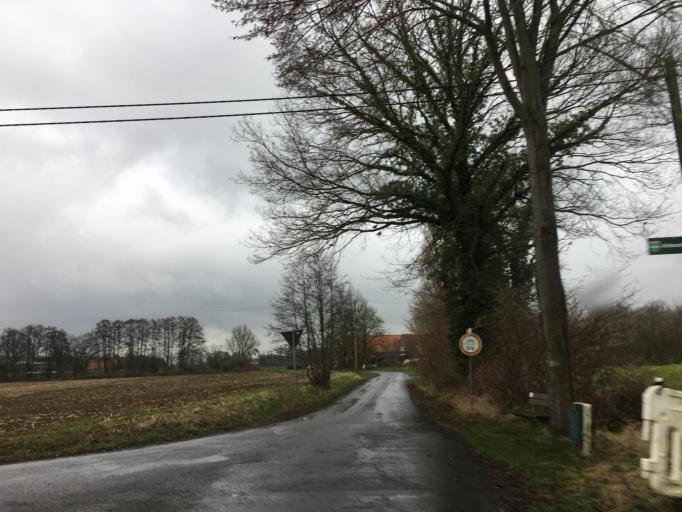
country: DE
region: North Rhine-Westphalia
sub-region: Regierungsbezirk Munster
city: Nordwalde
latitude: 52.0928
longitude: 7.5016
